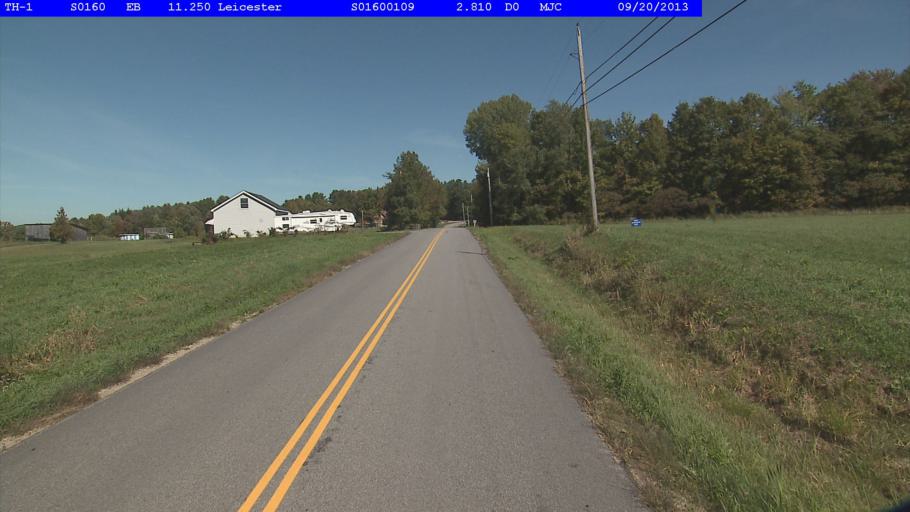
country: US
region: Vermont
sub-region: Rutland County
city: Brandon
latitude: 43.8634
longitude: -73.1126
